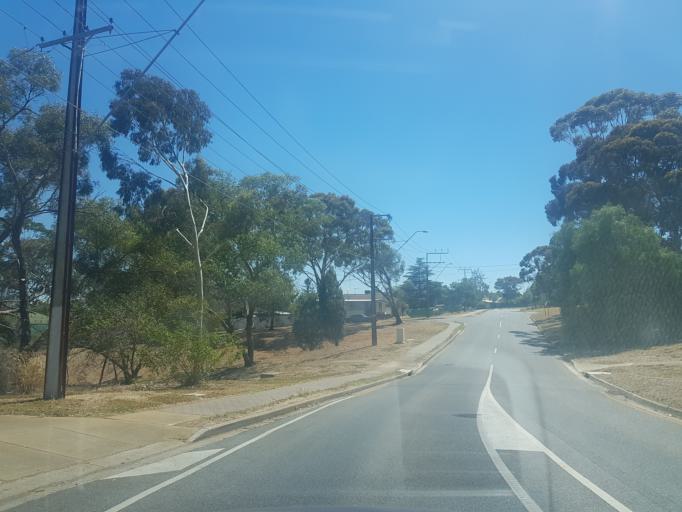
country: AU
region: South Australia
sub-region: Salisbury
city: Ingle Farm
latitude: -34.8164
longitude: 138.6520
